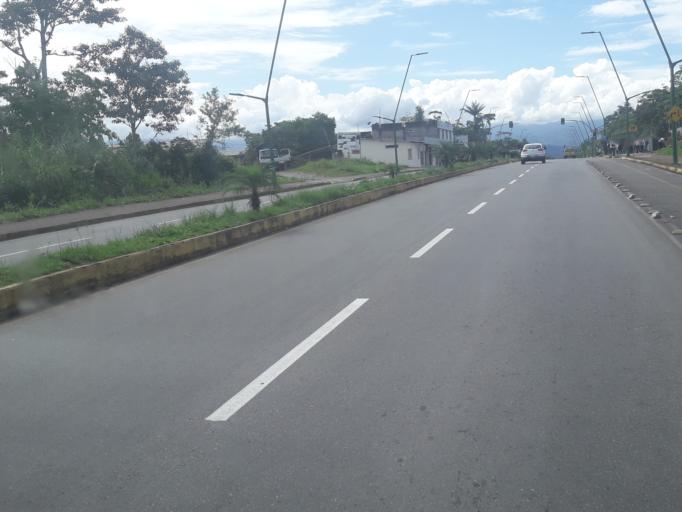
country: EC
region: Napo
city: Tena
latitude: -1.0194
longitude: -77.8064
